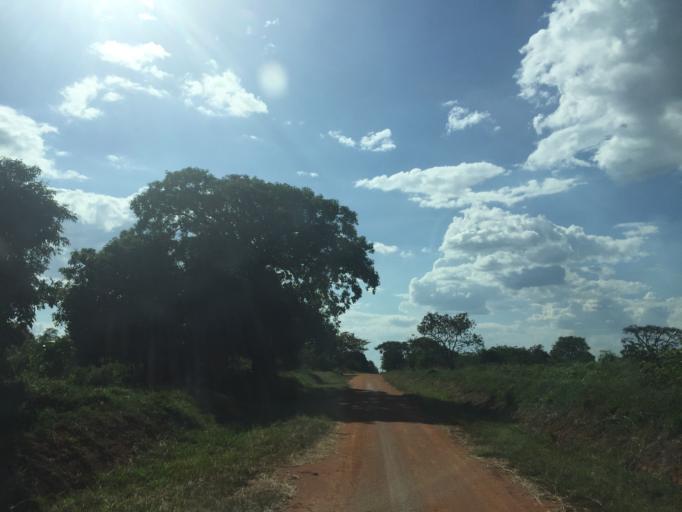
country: UG
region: Western Region
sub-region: Kiryandongo District
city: Masindi Port
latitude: 1.5285
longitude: 32.0932
